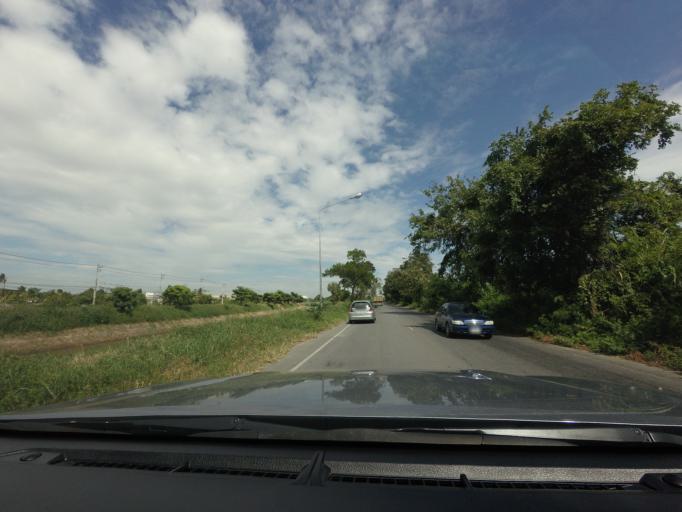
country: TH
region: Suphan Buri
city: Suphan Buri
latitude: 14.4630
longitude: 100.0902
